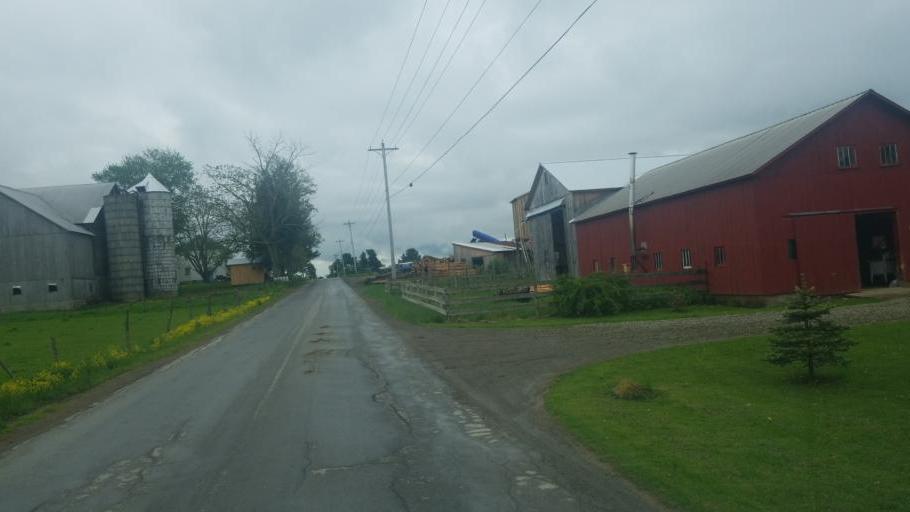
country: US
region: Pennsylvania
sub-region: Forest County
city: Tionesta
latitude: 41.4076
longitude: -79.3880
